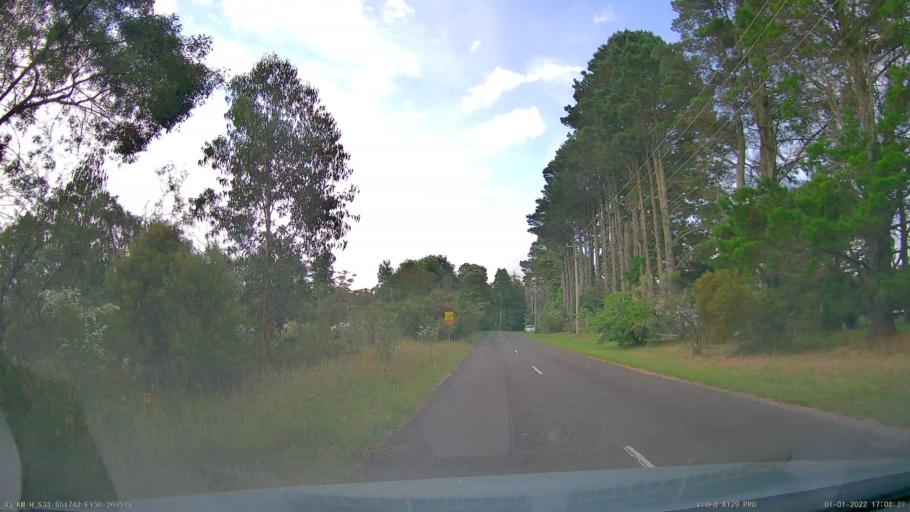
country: AU
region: New South Wales
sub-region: Blue Mountains Municipality
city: Blackheath
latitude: -33.6516
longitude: 150.2686
